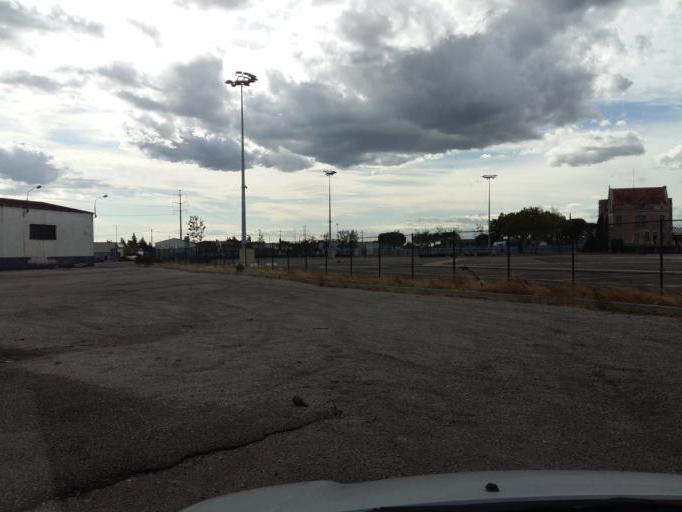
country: FR
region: Provence-Alpes-Cote d'Azur
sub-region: Departement du Vaucluse
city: Carpentras
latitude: 44.0335
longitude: 5.0437
